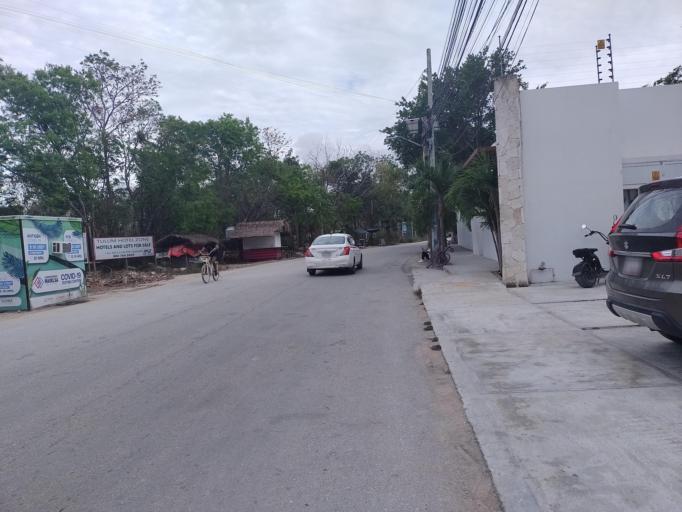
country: MX
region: Quintana Roo
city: Tulum
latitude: 20.2056
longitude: -87.4712
